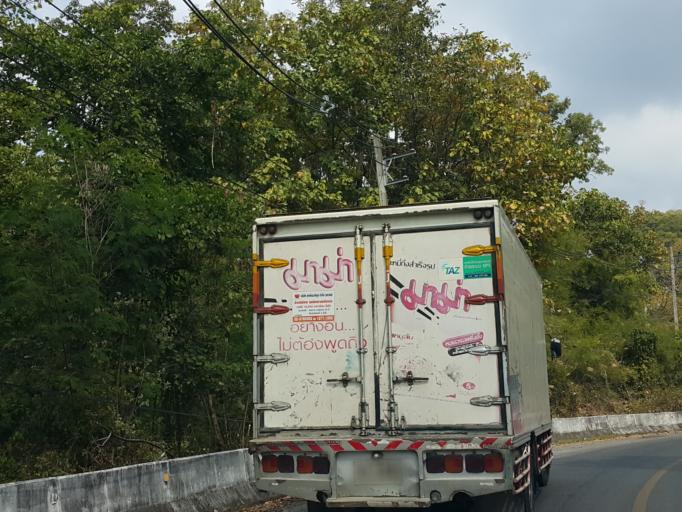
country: TH
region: Chiang Mai
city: Mae On
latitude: 18.8271
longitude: 99.2597
